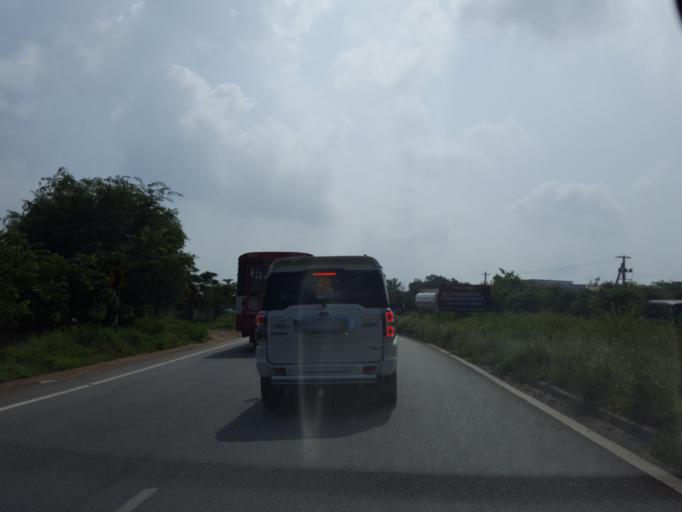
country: IN
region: Telangana
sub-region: Rangareddi
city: Ghatkesar
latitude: 17.2947
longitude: 78.7421
